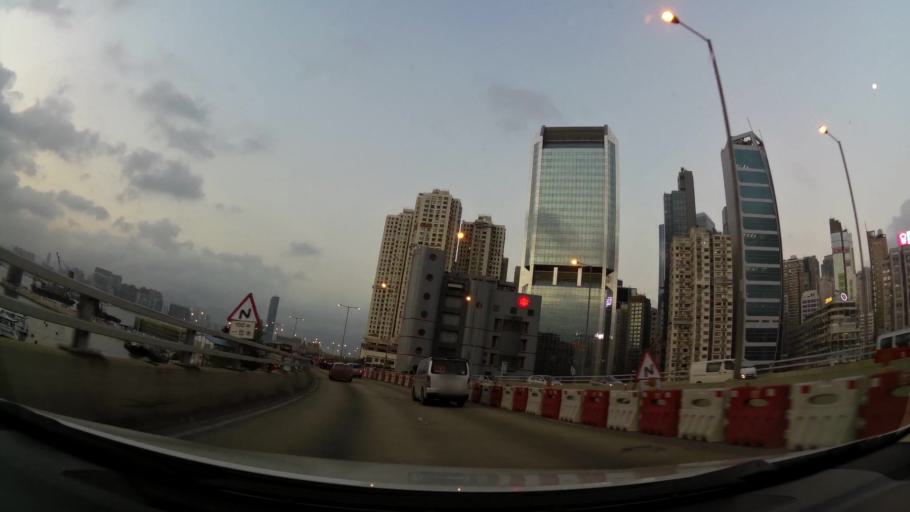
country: HK
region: Wanchai
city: Wan Chai
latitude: 22.2849
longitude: 114.1888
